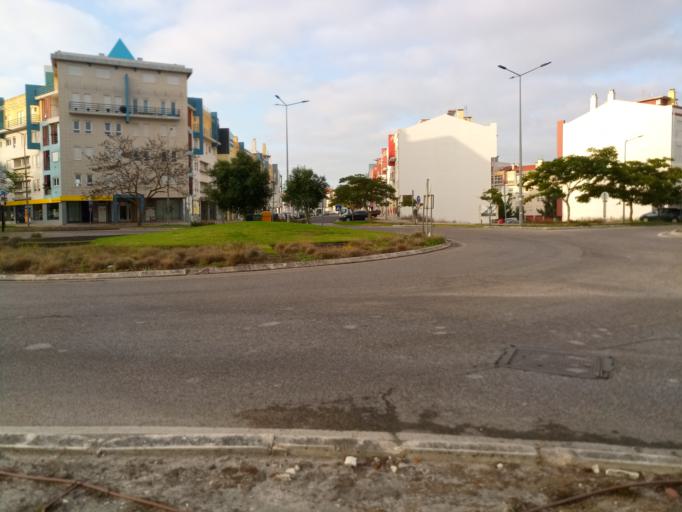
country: PT
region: Leiria
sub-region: Caldas da Rainha
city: Caldas da Rainha
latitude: 39.4135
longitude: -9.1460
